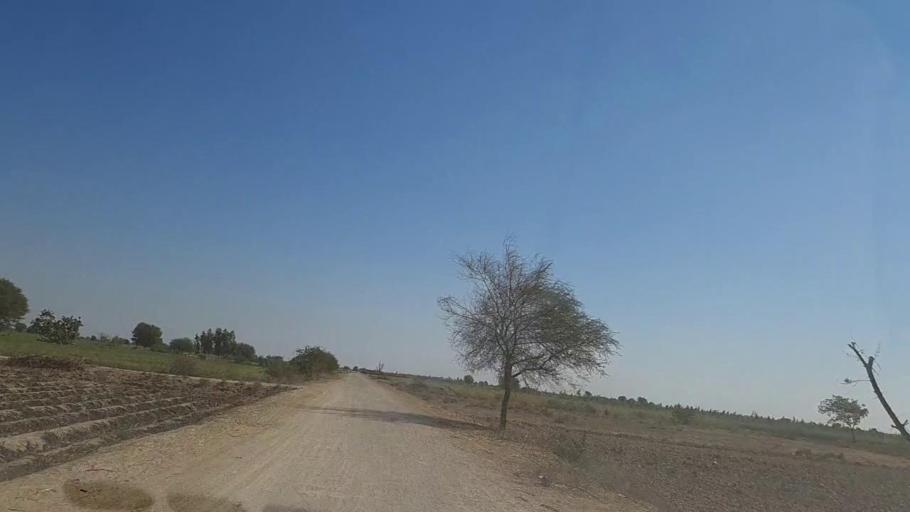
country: PK
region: Sindh
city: Digri
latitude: 25.1111
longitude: 69.1177
